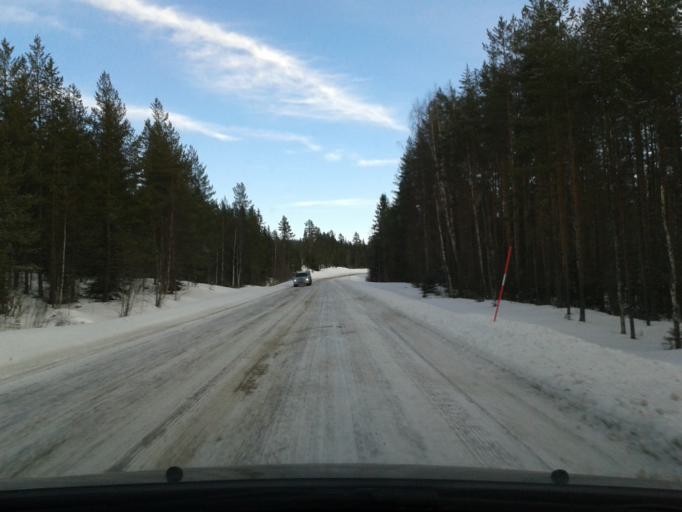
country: SE
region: Vaesterbotten
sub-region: Asele Kommun
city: Asele
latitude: 64.2064
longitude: 17.3282
